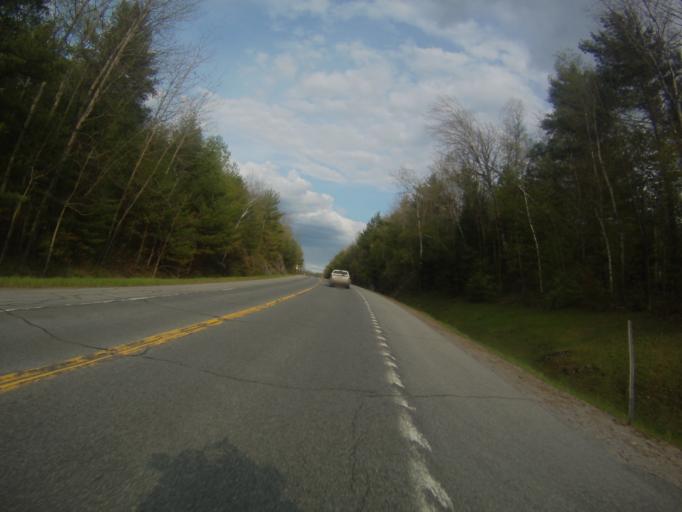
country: US
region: New York
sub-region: Warren County
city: Warrensburg
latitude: 43.6848
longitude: -73.9837
